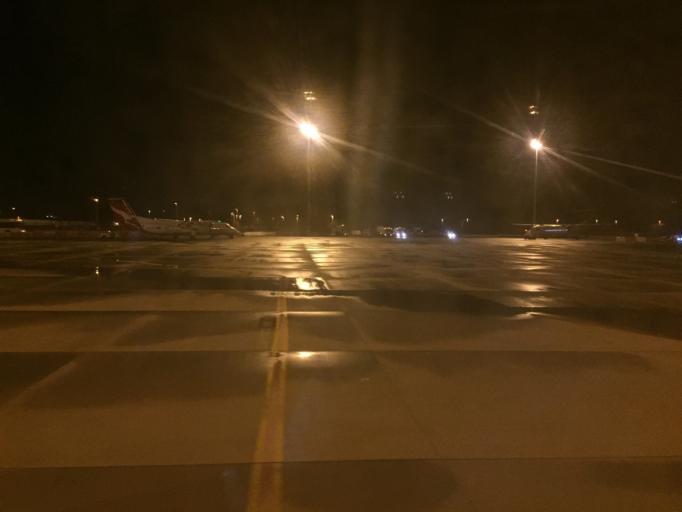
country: AU
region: Queensland
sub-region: Brisbane
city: Shorncliffe
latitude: -27.3820
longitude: 153.1224
